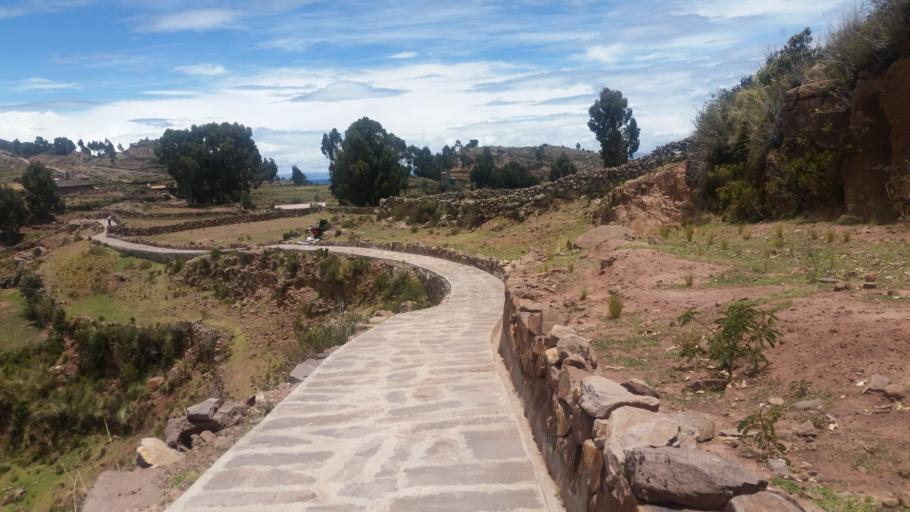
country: PE
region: Puno
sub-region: Provincia de Puno
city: Taquile
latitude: -15.7894
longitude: -69.6823
